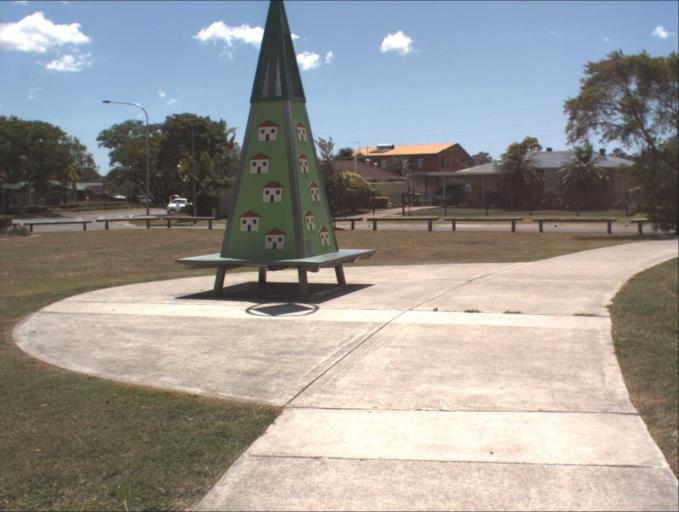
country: AU
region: Queensland
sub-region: Gold Coast
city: Yatala
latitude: -27.7268
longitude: 153.2113
